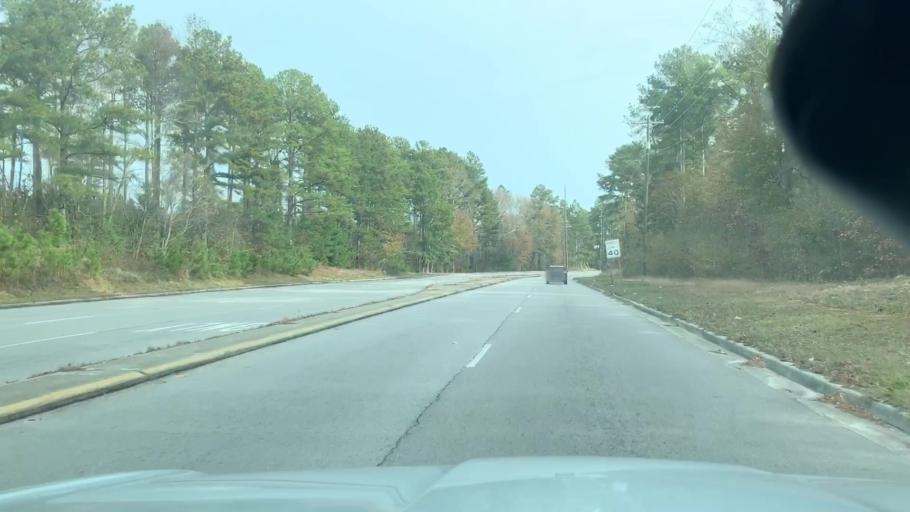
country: US
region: South Carolina
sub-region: Richland County
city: Dentsville
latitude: 34.0690
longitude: -80.9485
